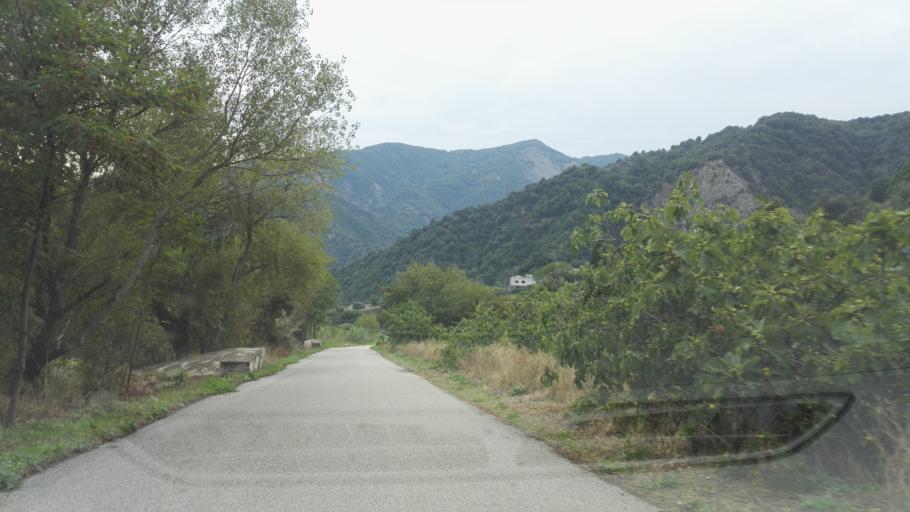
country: IT
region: Calabria
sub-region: Provincia di Reggio Calabria
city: Caulonia
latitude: 38.4276
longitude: 16.3902
